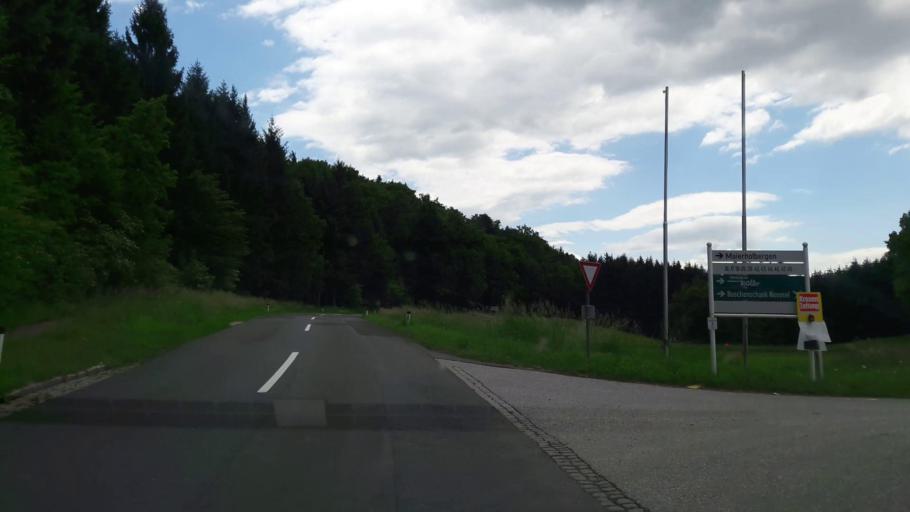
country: AT
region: Styria
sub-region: Politischer Bezirk Hartberg-Fuerstenfeld
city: Soechau
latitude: 47.0569
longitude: 16.0100
